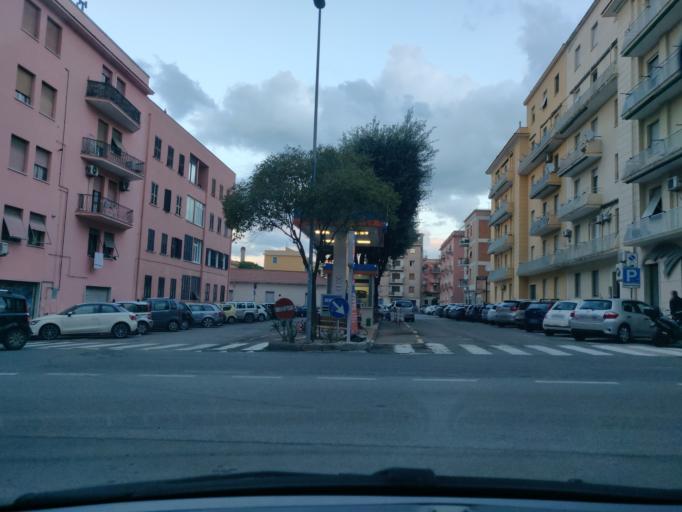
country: IT
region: Latium
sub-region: Citta metropolitana di Roma Capitale
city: Civitavecchia
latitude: 42.0947
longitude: 11.8001
